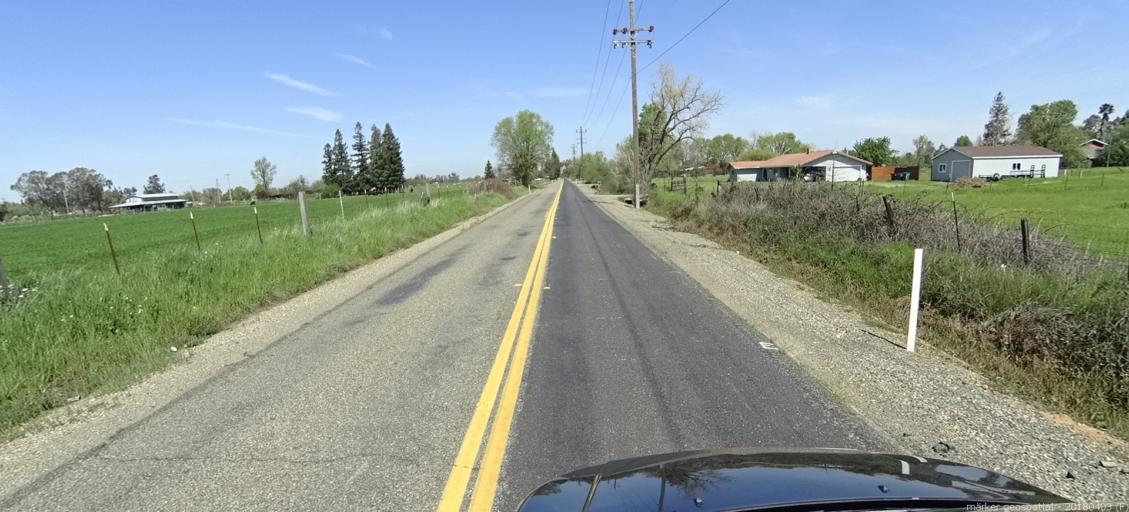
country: US
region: California
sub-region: Sacramento County
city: Wilton
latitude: 38.3929
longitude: -121.2739
